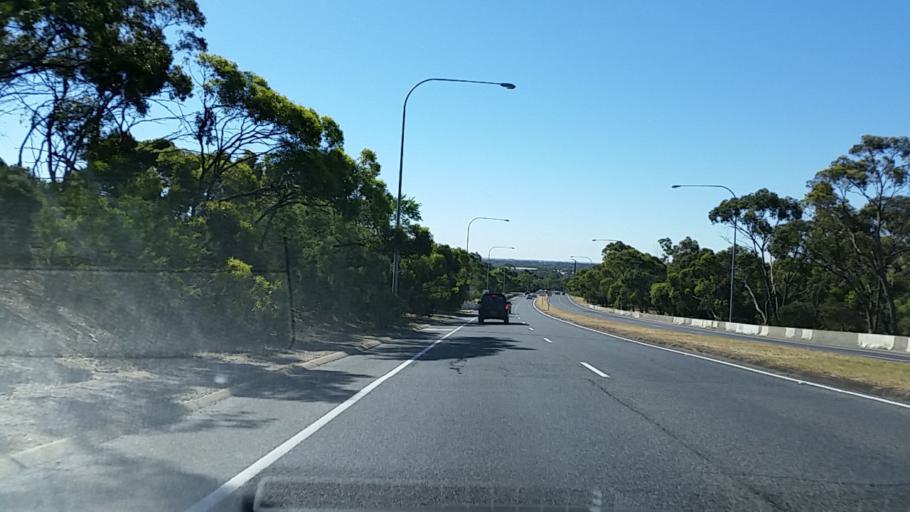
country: AU
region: South Australia
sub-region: Tea Tree Gully
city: Modbury
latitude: -34.8029
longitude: 138.6623
